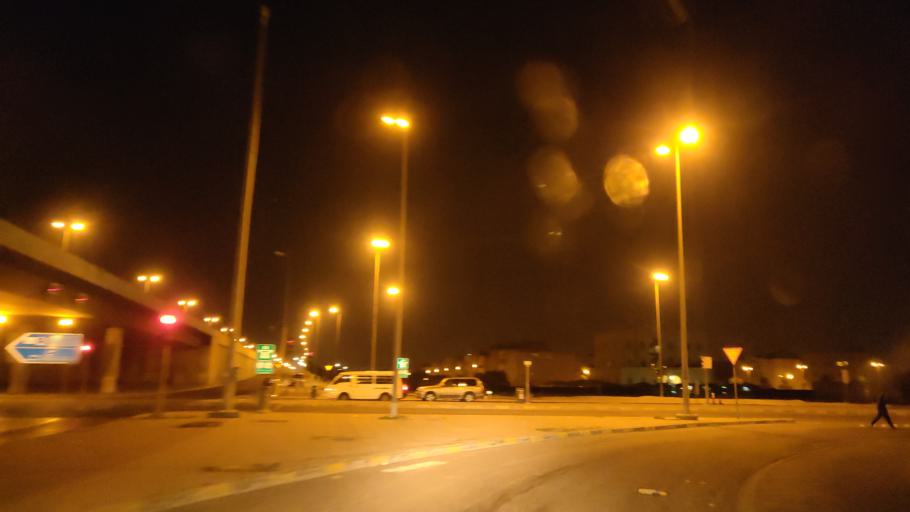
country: KW
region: Al Farwaniyah
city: Al Farwaniyah
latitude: 29.2671
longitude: 47.9405
